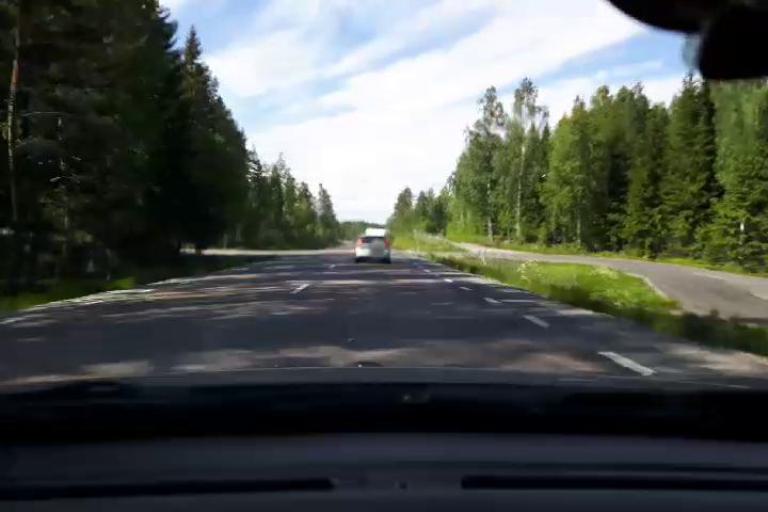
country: SE
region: Gaevleborg
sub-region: Bollnas Kommun
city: Kilafors
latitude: 61.2795
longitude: 16.5219
